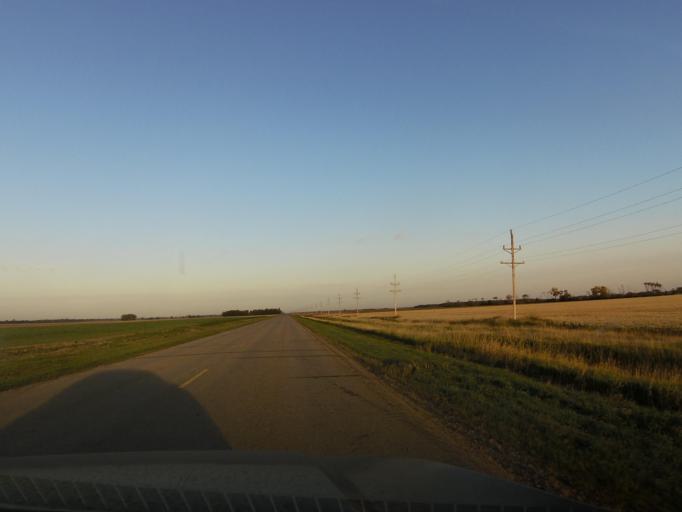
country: CA
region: Manitoba
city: Altona
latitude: 48.9634
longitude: -97.6068
